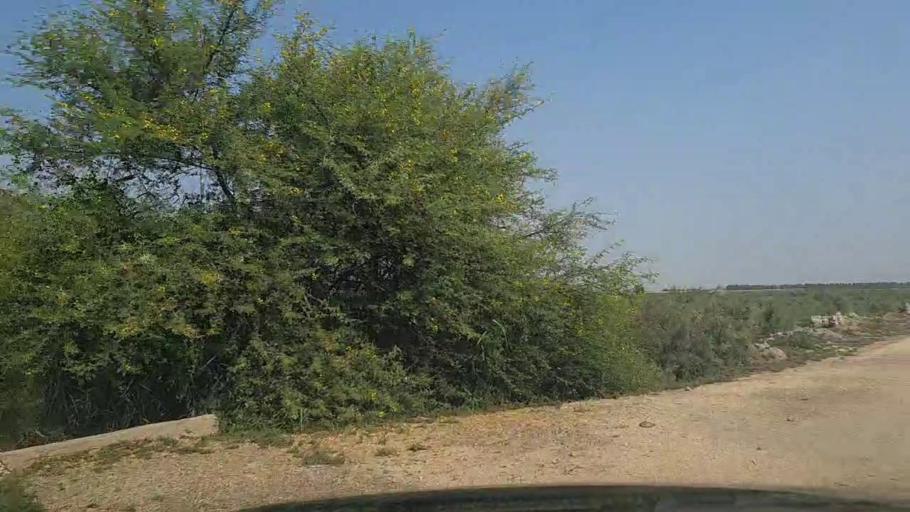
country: PK
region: Sindh
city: Mirpur Sakro
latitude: 24.6218
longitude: 67.7867
